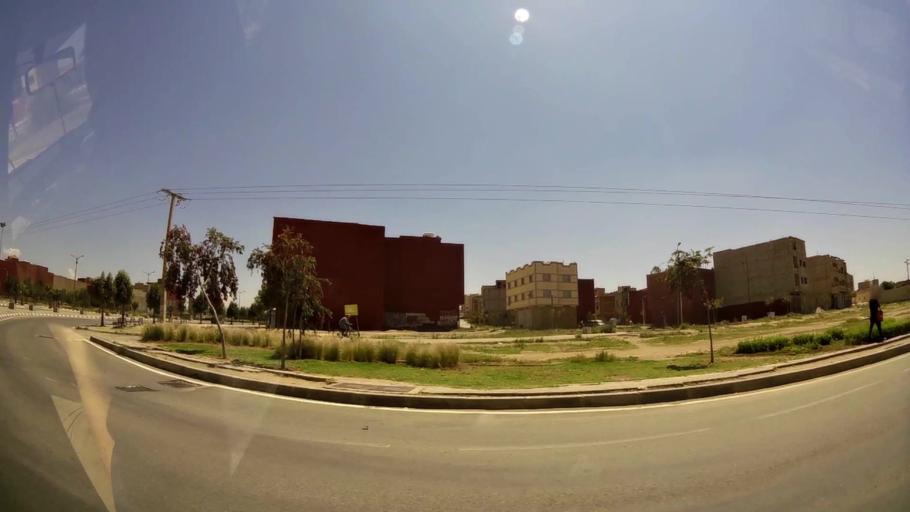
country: MA
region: Oriental
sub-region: Oujda-Angad
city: Oujda
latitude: 34.6828
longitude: -1.9468
